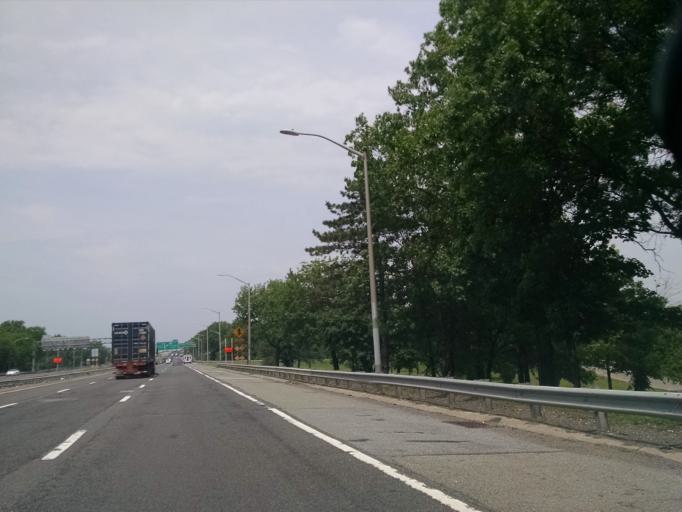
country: US
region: New York
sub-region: Richmond County
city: Bloomfield
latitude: 40.6107
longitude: -74.1515
